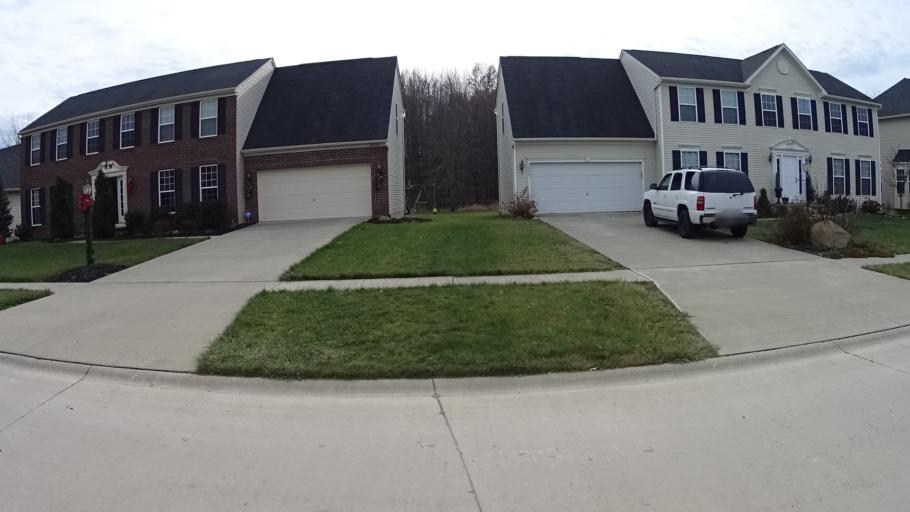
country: US
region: Ohio
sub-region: Lorain County
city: North Ridgeville
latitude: 41.4043
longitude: -82.0217
